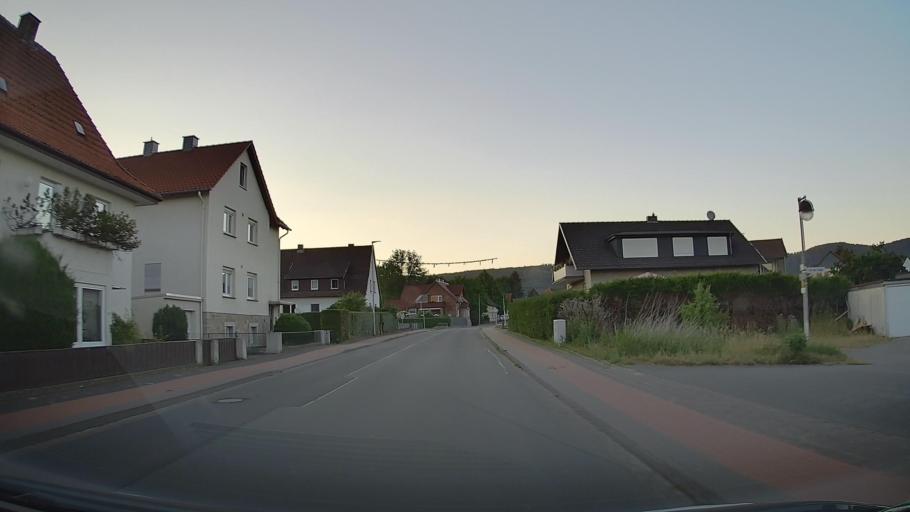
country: DE
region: Lower Saxony
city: Bad Pyrmont
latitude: 51.9842
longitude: 9.2306
